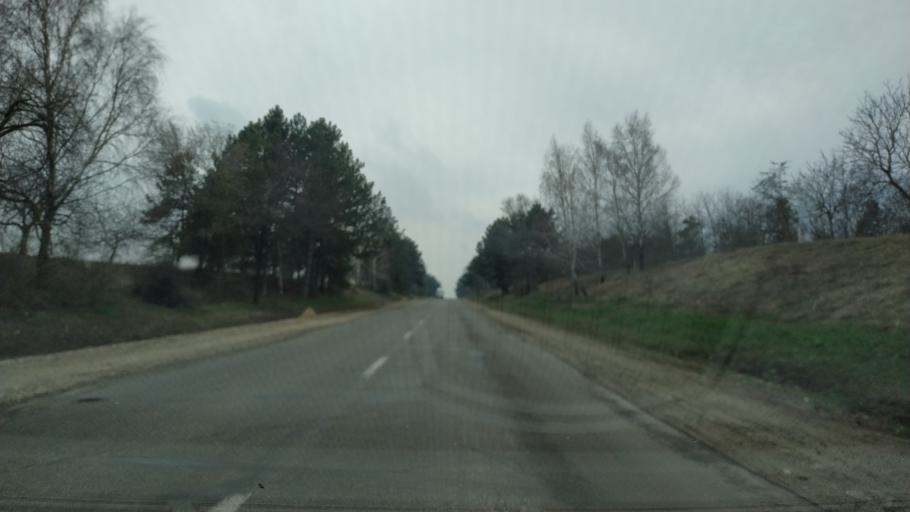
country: MD
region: Cahul
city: Cahul
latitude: 45.9413
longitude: 28.2932
